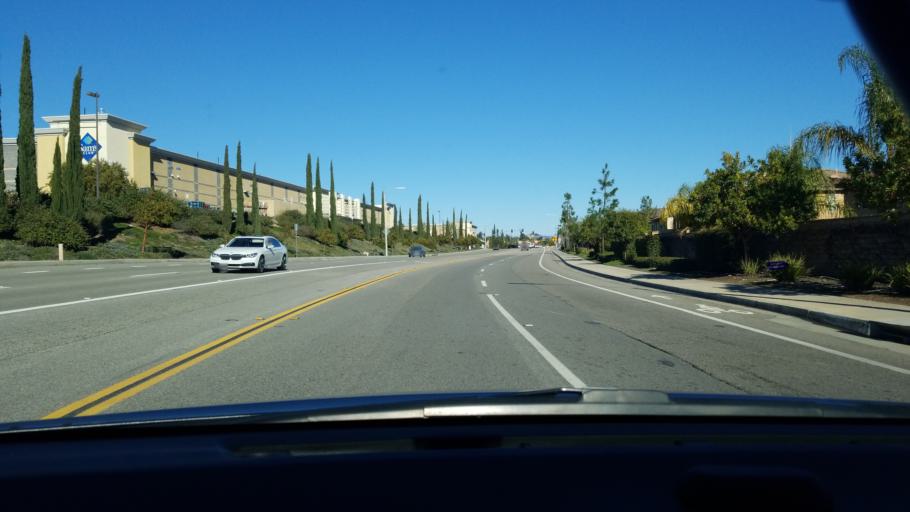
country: US
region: California
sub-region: Riverside County
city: Murrieta Hot Springs
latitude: 33.5514
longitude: -117.1783
